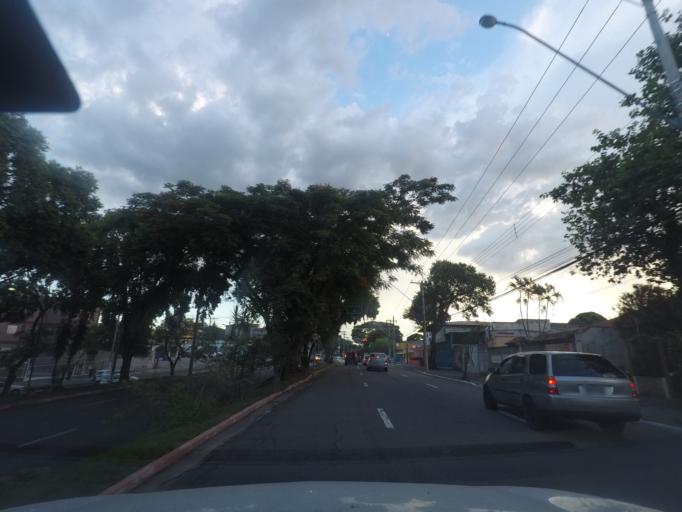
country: BR
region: Sao Paulo
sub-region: Sao Jose Dos Campos
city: Sao Jose dos Campos
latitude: -23.2288
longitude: -45.8802
